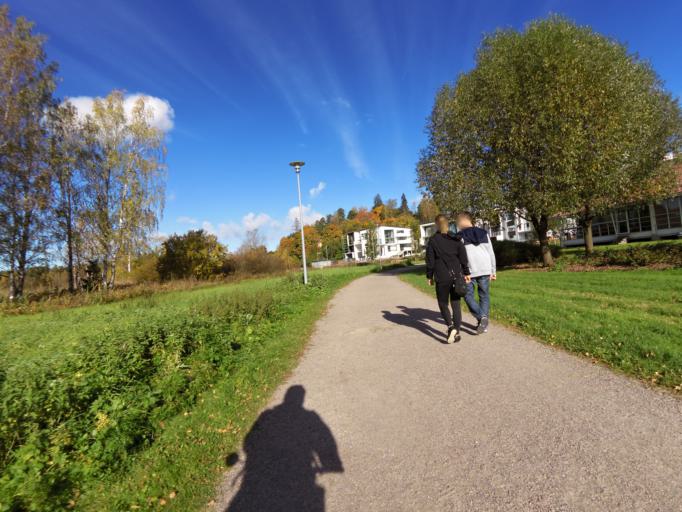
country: FI
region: Uusimaa
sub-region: Helsinki
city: Espoo
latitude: 60.1613
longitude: 24.6117
